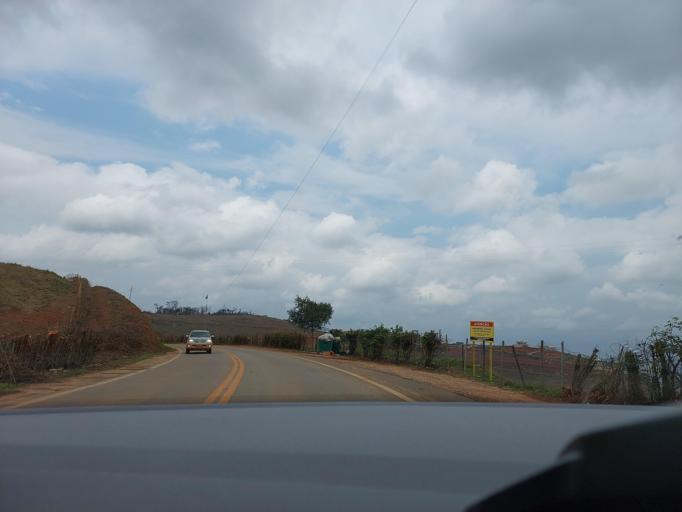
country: BR
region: Minas Gerais
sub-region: Ponte Nova
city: Ponte Nova
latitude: -20.3880
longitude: -42.8716
